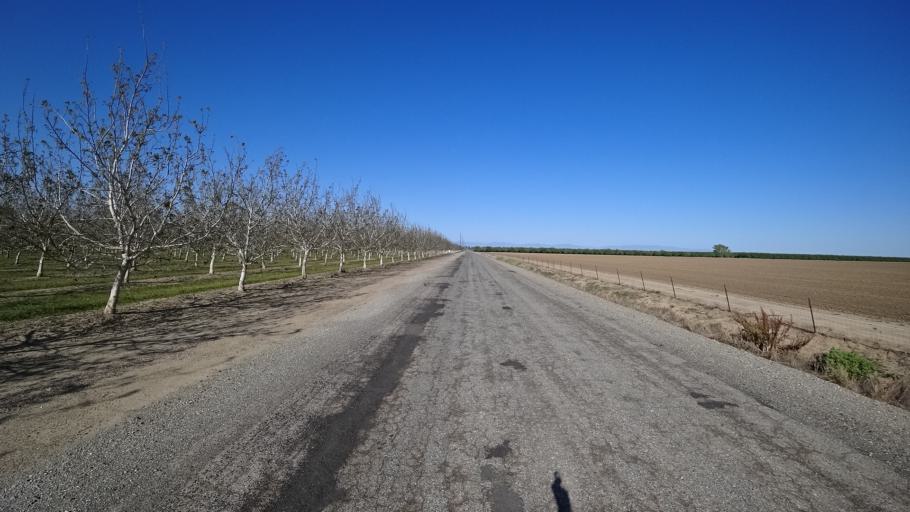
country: US
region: California
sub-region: Glenn County
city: Hamilton City
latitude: 39.6782
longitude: -122.0493
